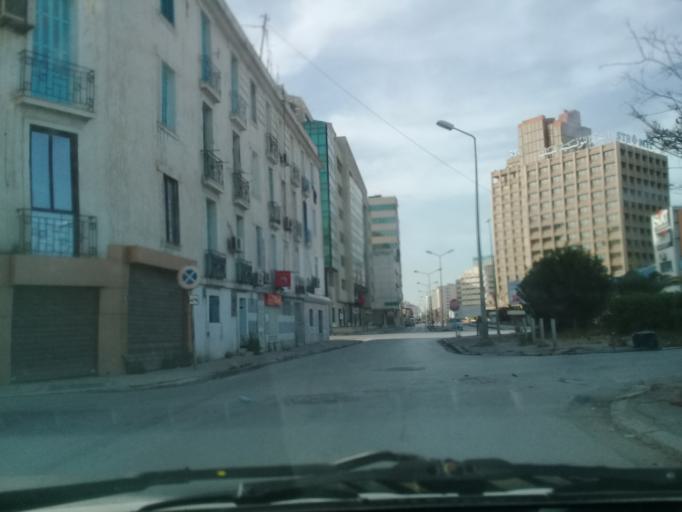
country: TN
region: Tunis
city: Tunis
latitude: 36.8060
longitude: 10.1844
